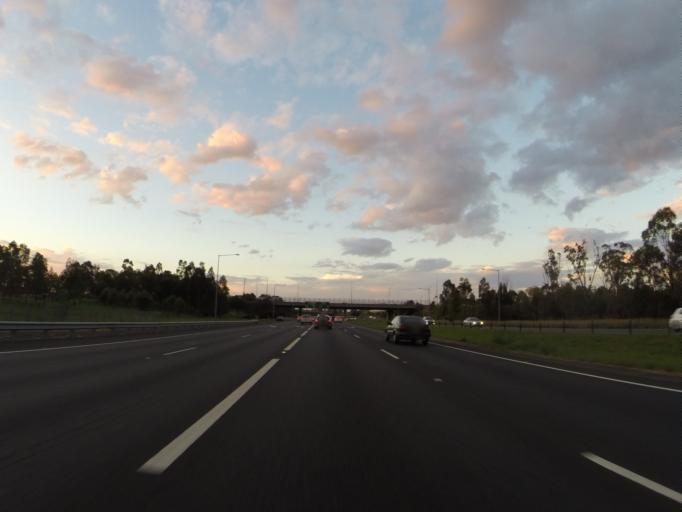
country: AU
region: New South Wales
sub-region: Campbelltown Municipality
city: Glenfield
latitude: -33.9587
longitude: 150.8762
